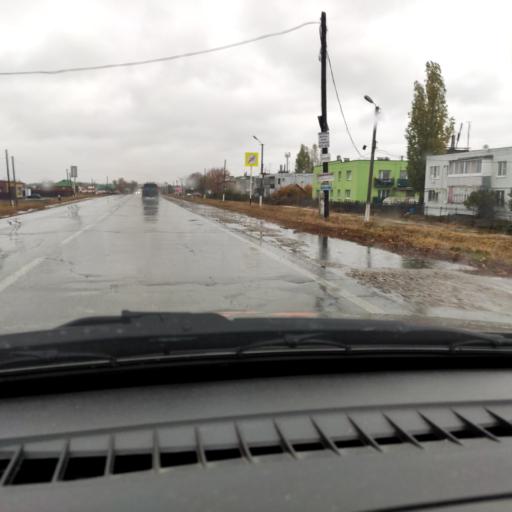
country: RU
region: Samara
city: Tol'yatti
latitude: 53.6416
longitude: 49.2965
